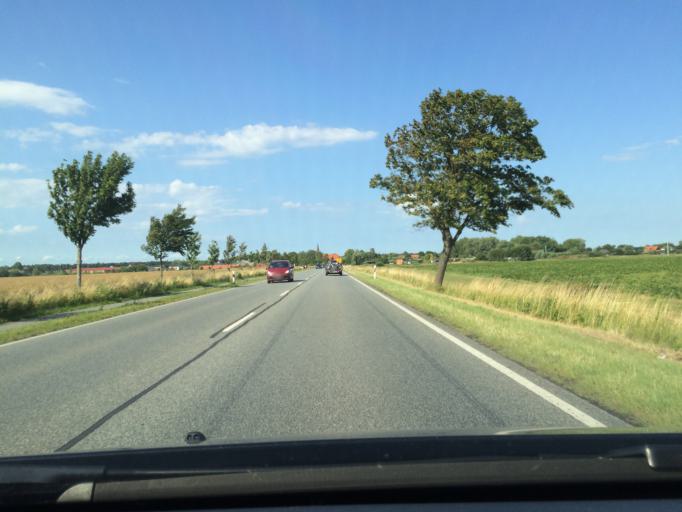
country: DE
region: Mecklenburg-Vorpommern
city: Rovershagen
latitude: 54.1679
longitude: 12.2383
